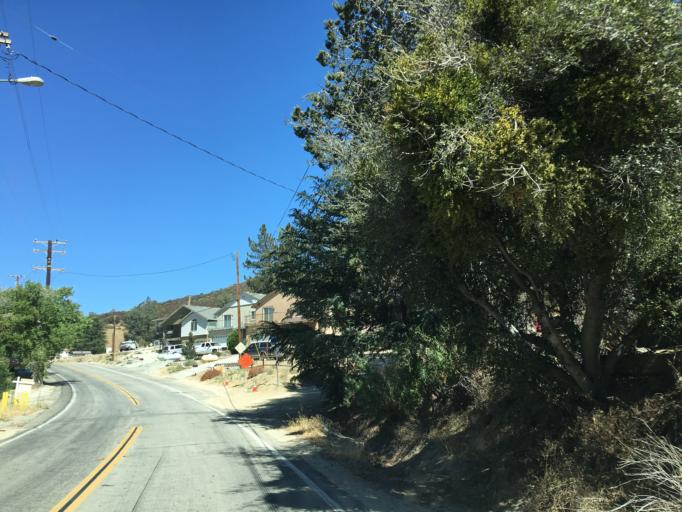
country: US
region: California
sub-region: Los Angeles County
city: Green Valley
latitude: 34.6768
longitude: -118.4452
